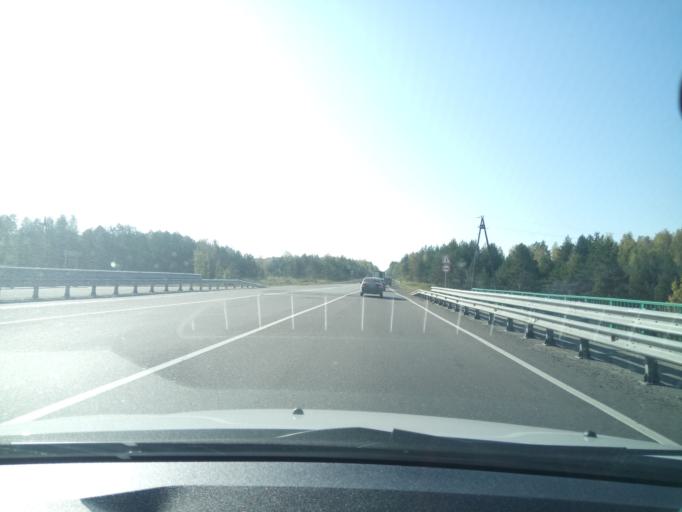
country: RU
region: Nizjnij Novgorod
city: Dal'neye Konstantinovo
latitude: 55.9595
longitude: 43.9756
